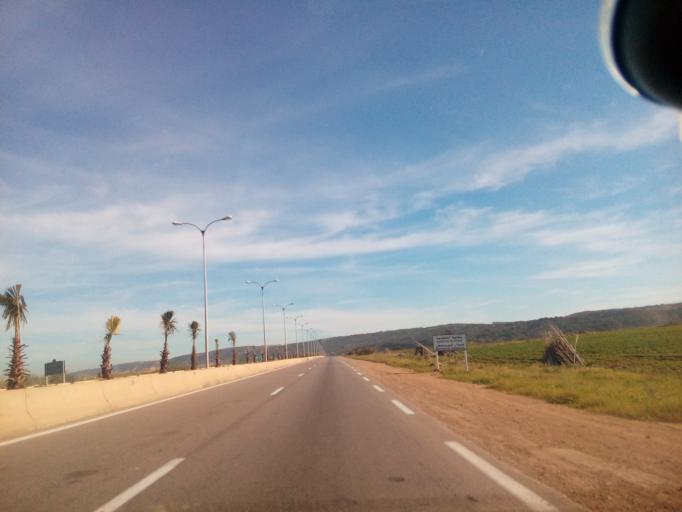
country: DZ
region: Mostaganem
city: Mostaganem
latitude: 35.8374
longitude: -0.0018
